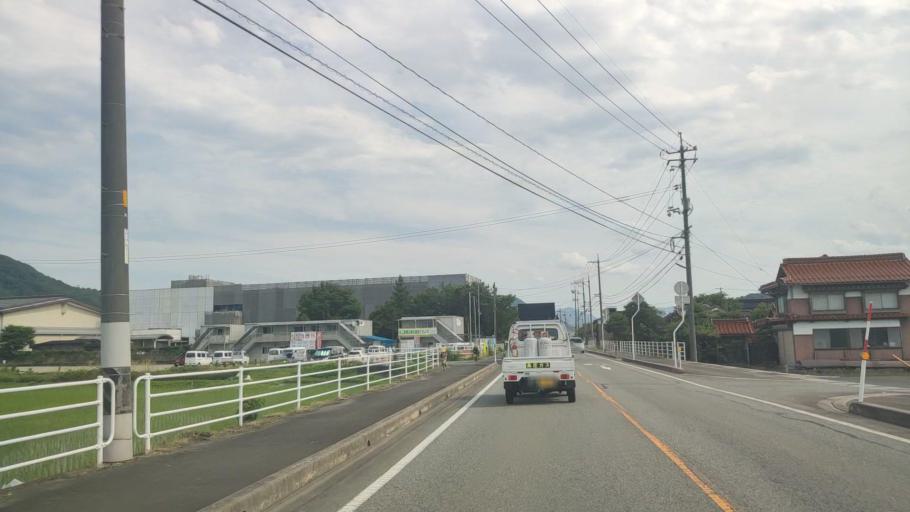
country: JP
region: Tottori
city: Tottori
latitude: 35.4554
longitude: 134.2032
